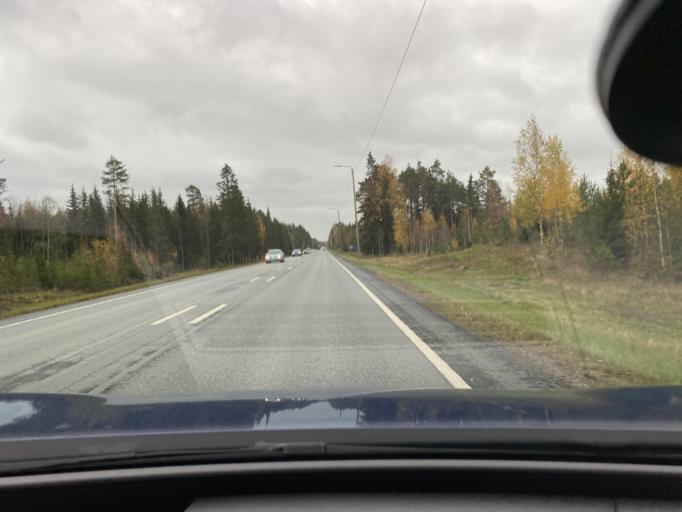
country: FI
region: Varsinais-Suomi
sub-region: Vakka-Suomi
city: Laitila
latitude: 60.9533
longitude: 21.5974
